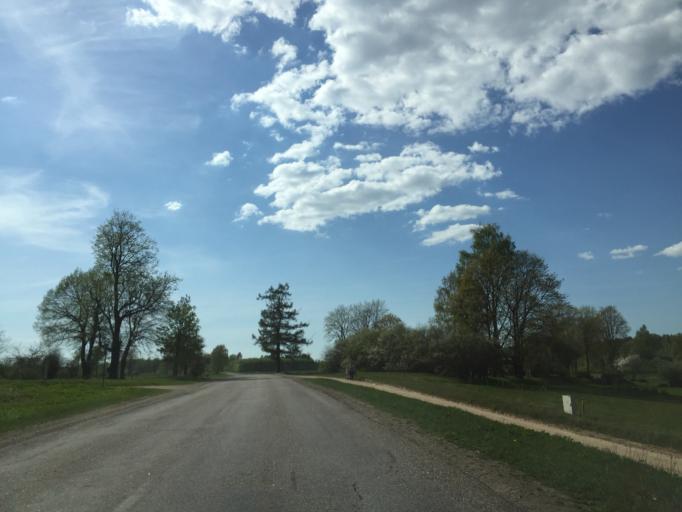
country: LV
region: Limbazu Rajons
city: Limbazi
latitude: 57.5132
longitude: 24.7889
